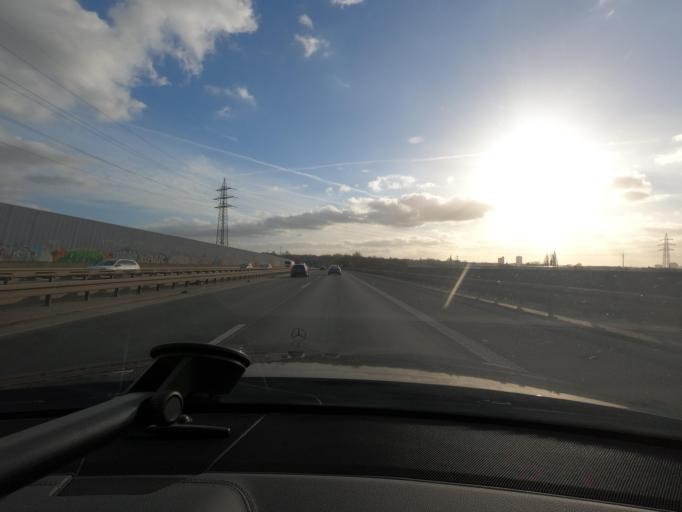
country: DE
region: North Rhine-Westphalia
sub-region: Regierungsbezirk Arnsberg
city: Dortmund
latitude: 51.5268
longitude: 7.5166
